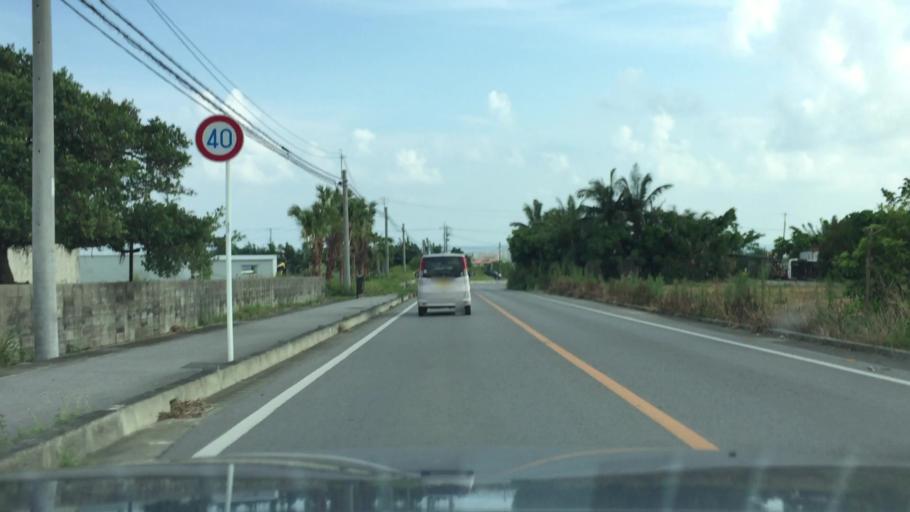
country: JP
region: Okinawa
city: Ishigaki
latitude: 24.3540
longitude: 124.1740
